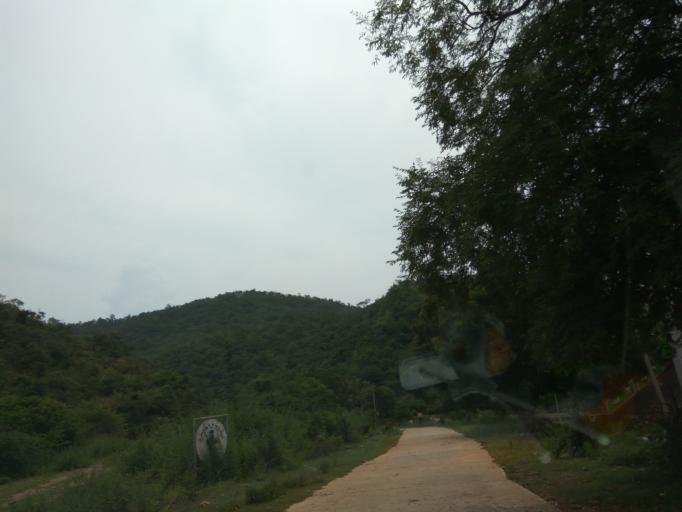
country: IN
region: Andhra Pradesh
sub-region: Prakasam
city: Cumbum
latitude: 15.4437
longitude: 79.0821
